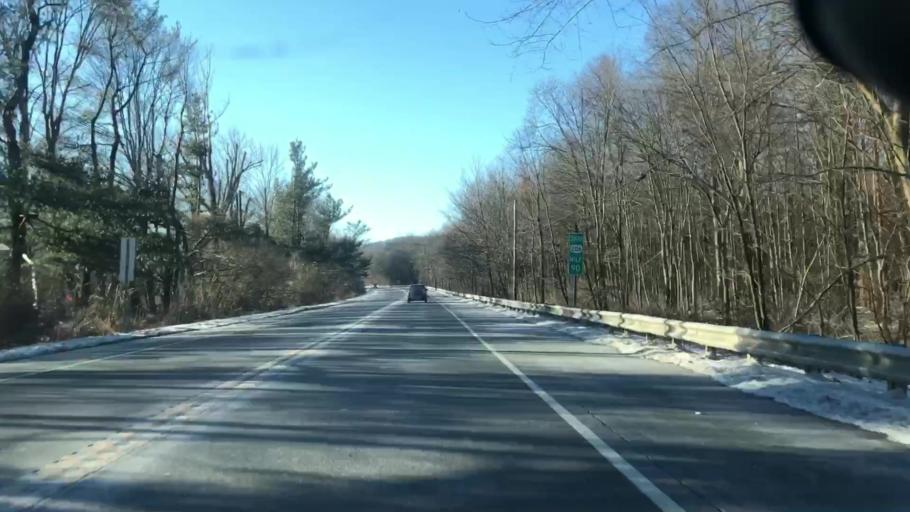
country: US
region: New Jersey
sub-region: Morris County
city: Chester
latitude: 40.8203
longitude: -74.7100
